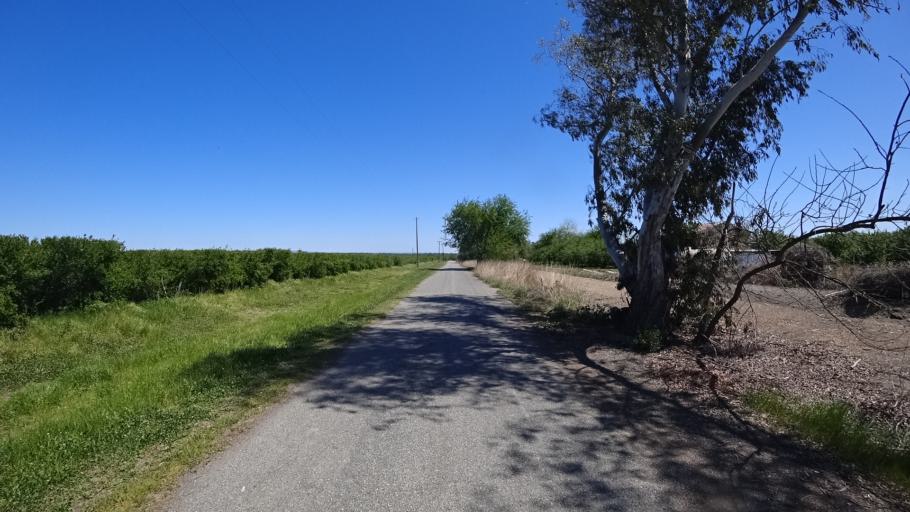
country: US
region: California
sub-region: Glenn County
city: Hamilton City
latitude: 39.7287
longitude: -122.0919
